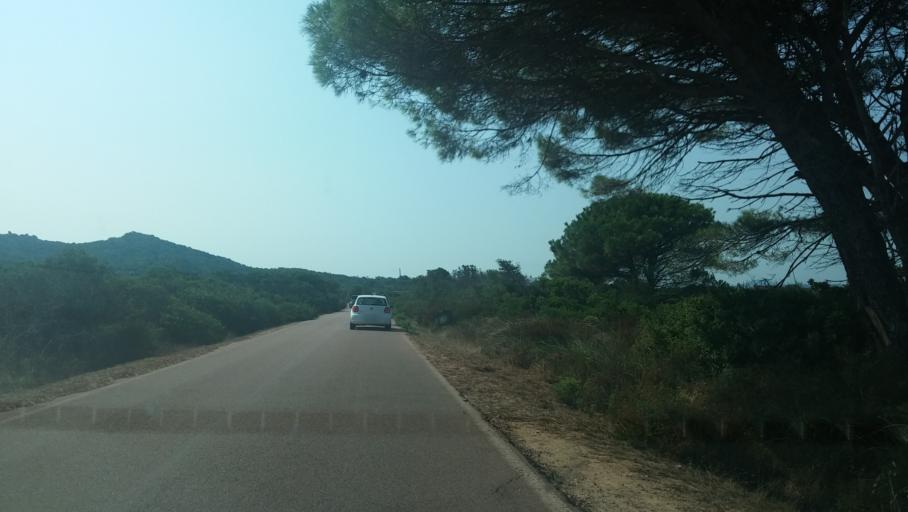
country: IT
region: Sardinia
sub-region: Provincia di Olbia-Tempio
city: La Maddalena
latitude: 41.1980
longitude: 9.4574
